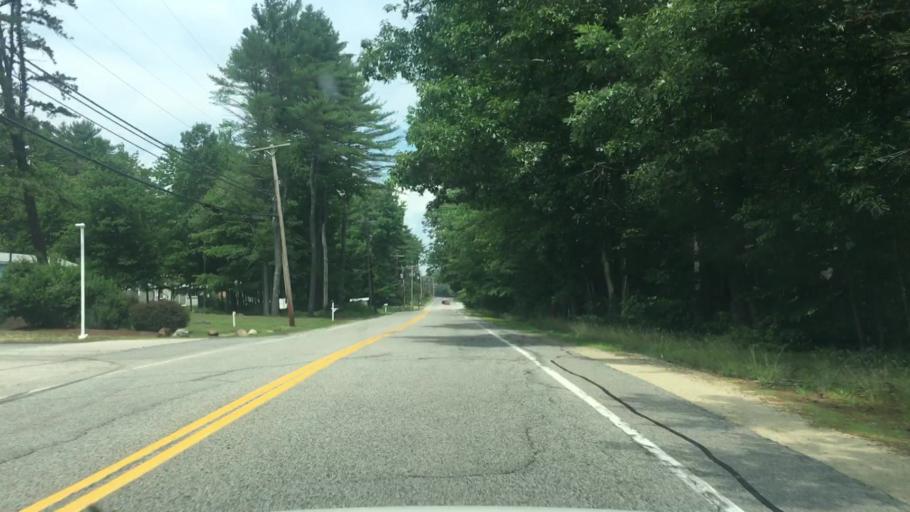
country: US
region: New Hampshire
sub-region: Strafford County
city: Rochester
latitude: 43.3594
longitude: -70.9803
